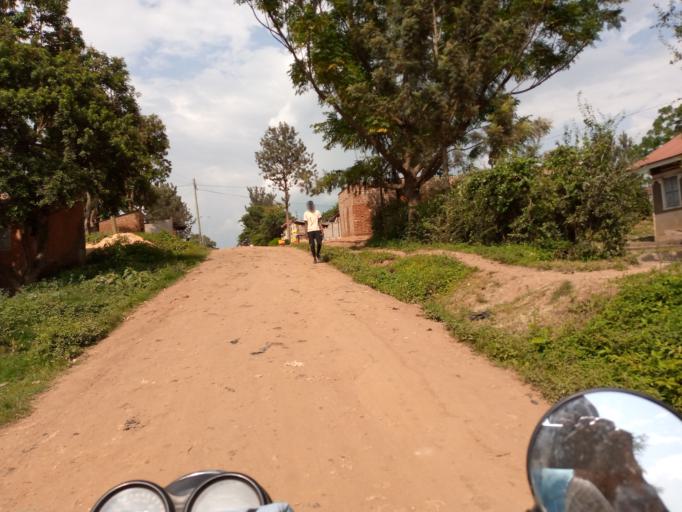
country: UG
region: Eastern Region
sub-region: Mbale District
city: Mbale
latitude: 1.0833
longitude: 34.1676
